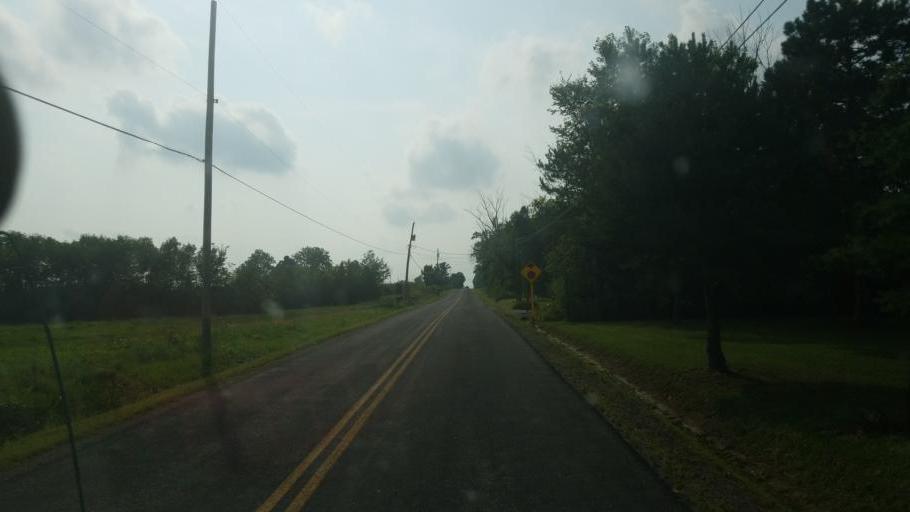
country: US
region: Ohio
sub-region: Medina County
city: Westfield Center
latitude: 41.0518
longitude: -81.9360
